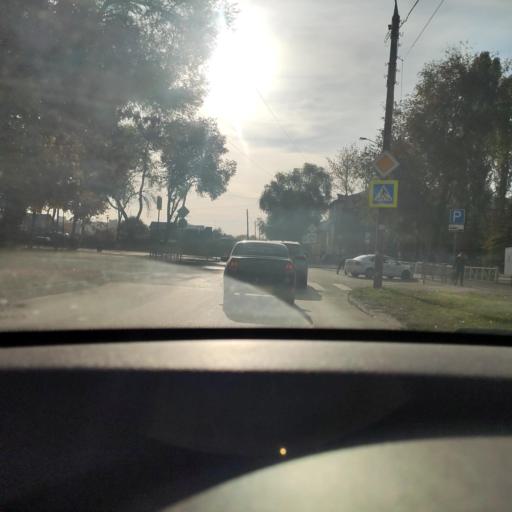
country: RU
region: Samara
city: Samara
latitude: 53.2251
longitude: 50.2448
